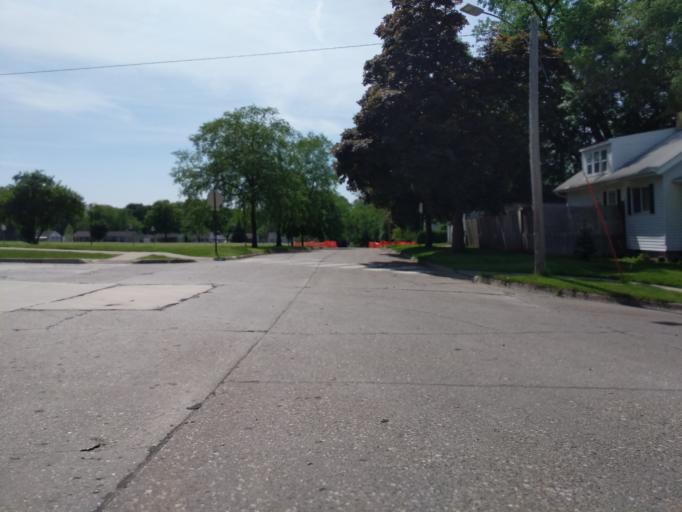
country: US
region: Iowa
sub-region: Linn County
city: Cedar Rapids
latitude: 42.0172
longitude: -91.6408
